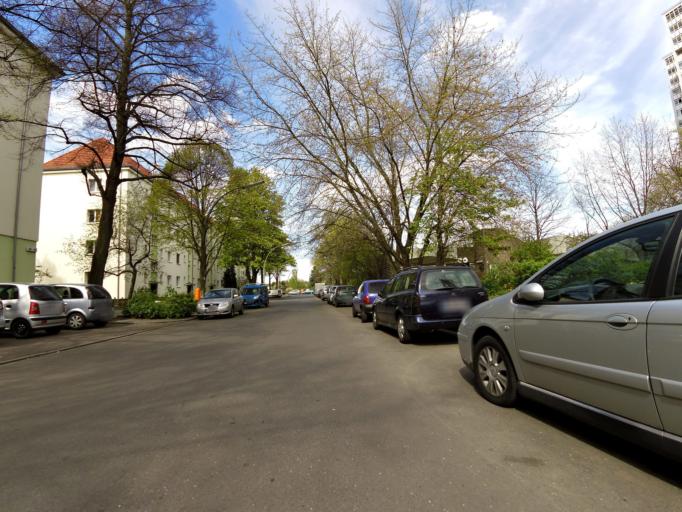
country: DE
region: Berlin
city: Plaenterwald
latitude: 52.4763
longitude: 13.4646
